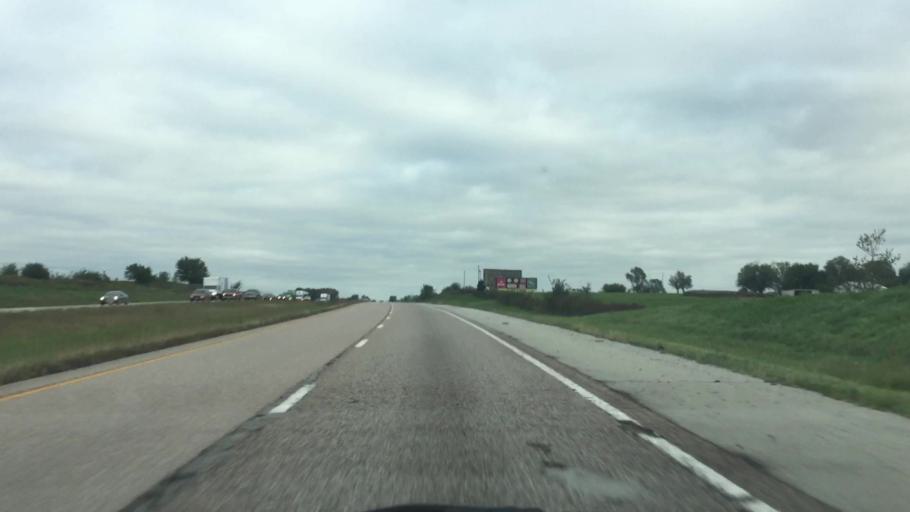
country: US
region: Missouri
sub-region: Clinton County
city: Lathrop
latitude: 39.5214
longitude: -94.2817
